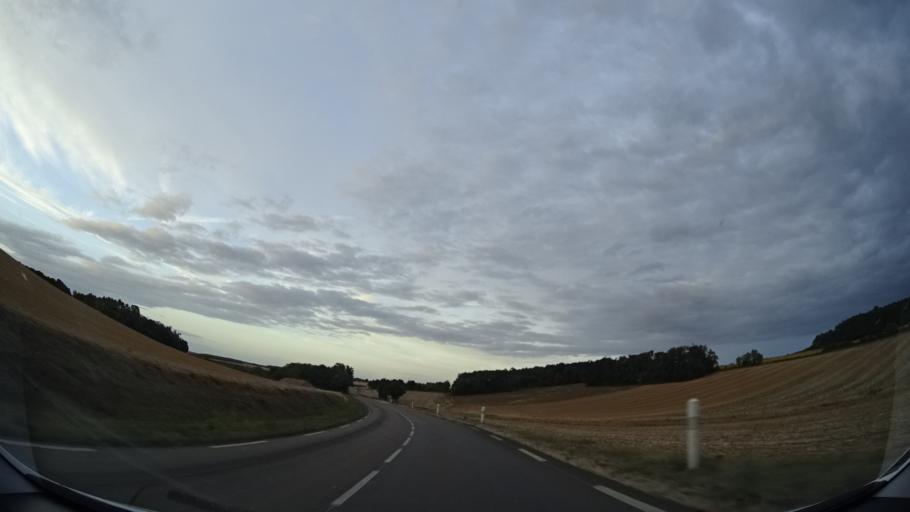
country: FR
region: Bourgogne
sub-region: Departement de l'Yonne
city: Saint-Julien-du-Sault
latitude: 47.9312
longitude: 3.2248
